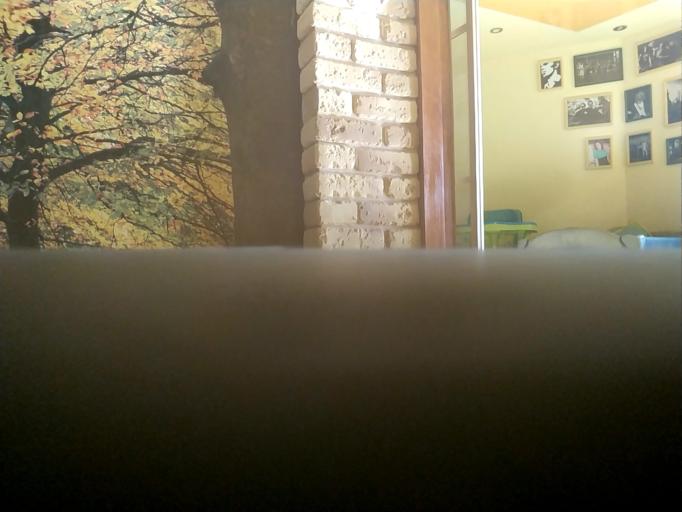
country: RU
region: Smolensk
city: Temkino
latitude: 54.9936
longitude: 34.9401
